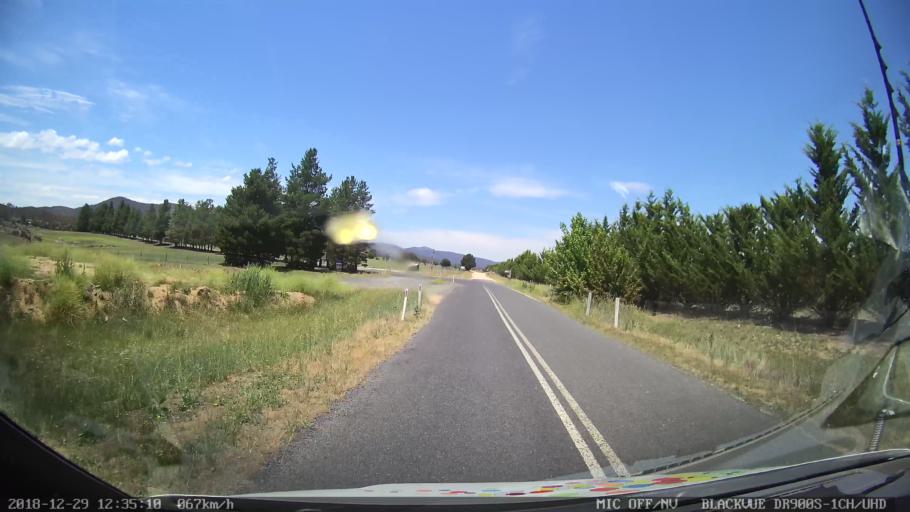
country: AU
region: Australian Capital Territory
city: Macarthur
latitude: -35.5595
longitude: 149.2226
